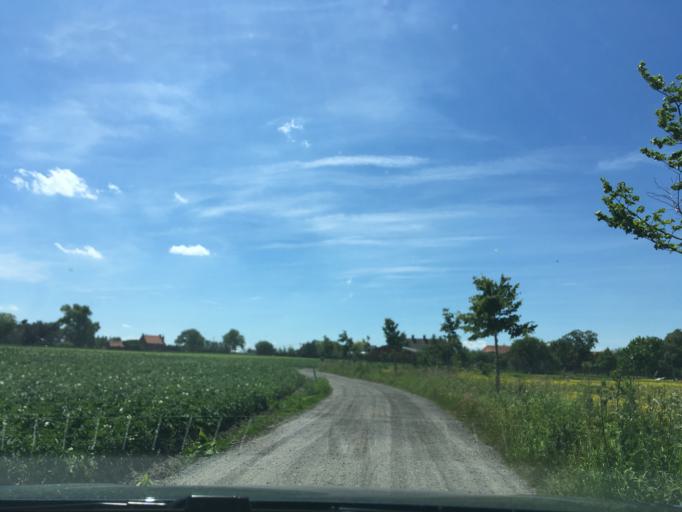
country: BE
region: Flanders
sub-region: Provincie West-Vlaanderen
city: Lichtervelde
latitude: 51.0346
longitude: 3.1199
